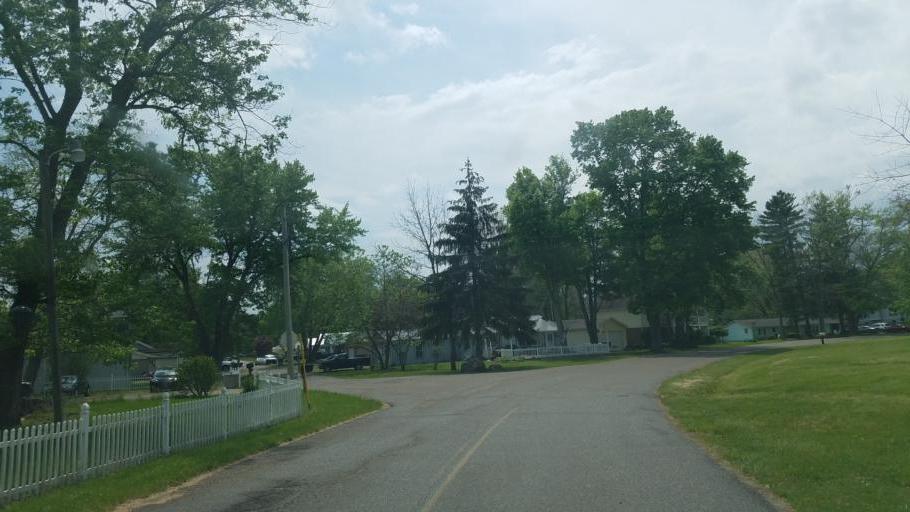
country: US
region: Ohio
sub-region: Fairfield County
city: Fairfield Beach
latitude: 39.9207
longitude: -82.4722
